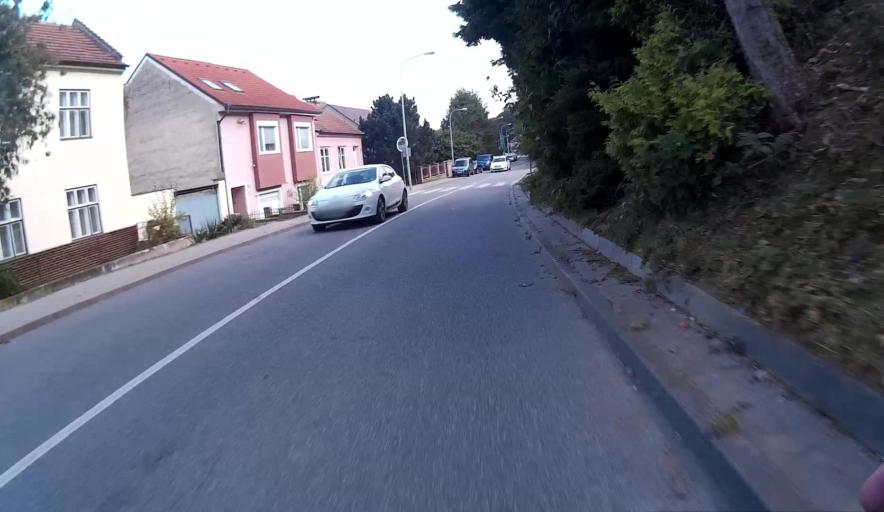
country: CZ
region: South Moravian
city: Podoli
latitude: 49.2028
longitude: 16.7150
